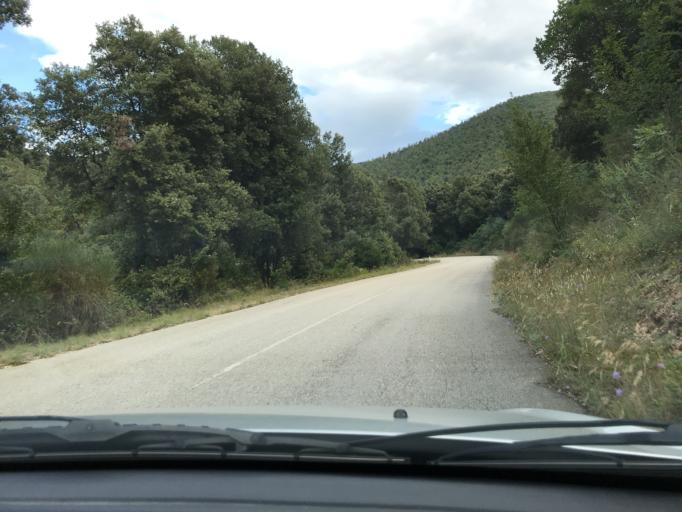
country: IT
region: Umbria
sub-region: Provincia di Terni
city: Montecchio
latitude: 42.6818
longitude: 12.3005
